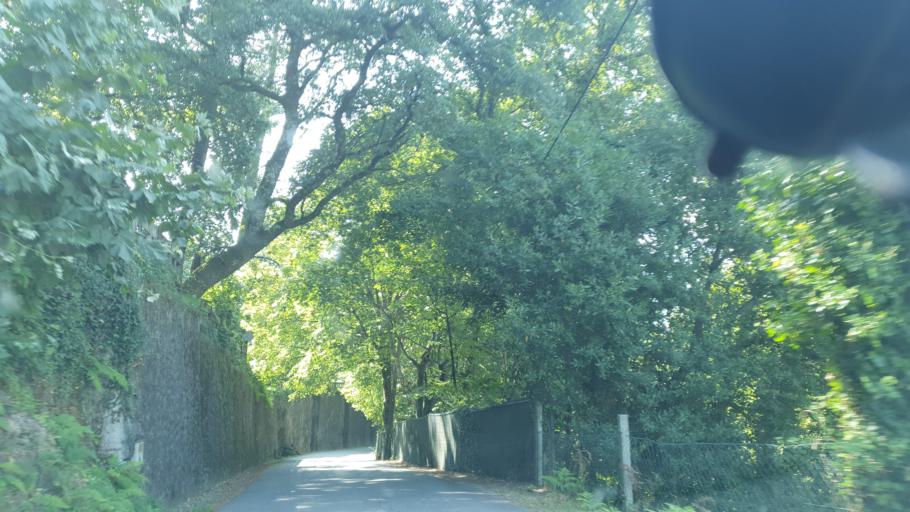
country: PT
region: Braga
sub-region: Vieira do Minho
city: Real
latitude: 41.6702
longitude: -8.1747
